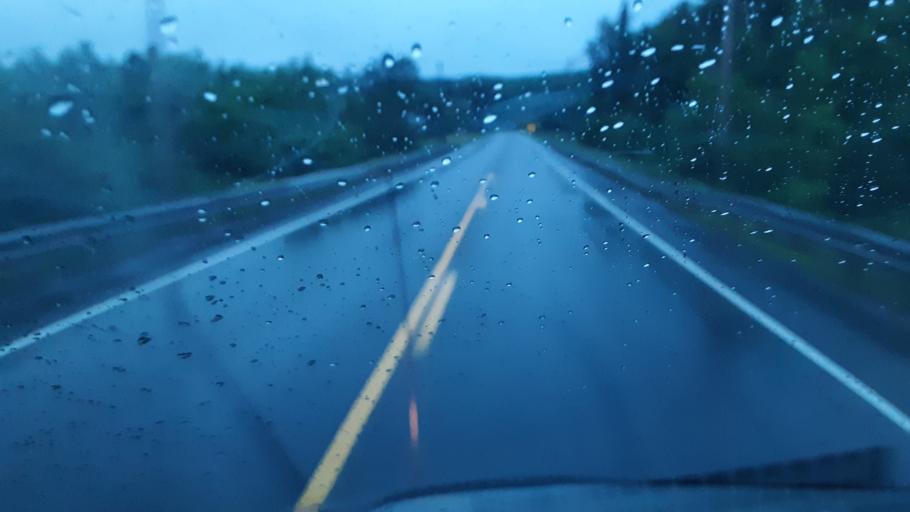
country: US
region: Maine
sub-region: Penobscot County
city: Patten
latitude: 45.8927
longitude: -68.4240
